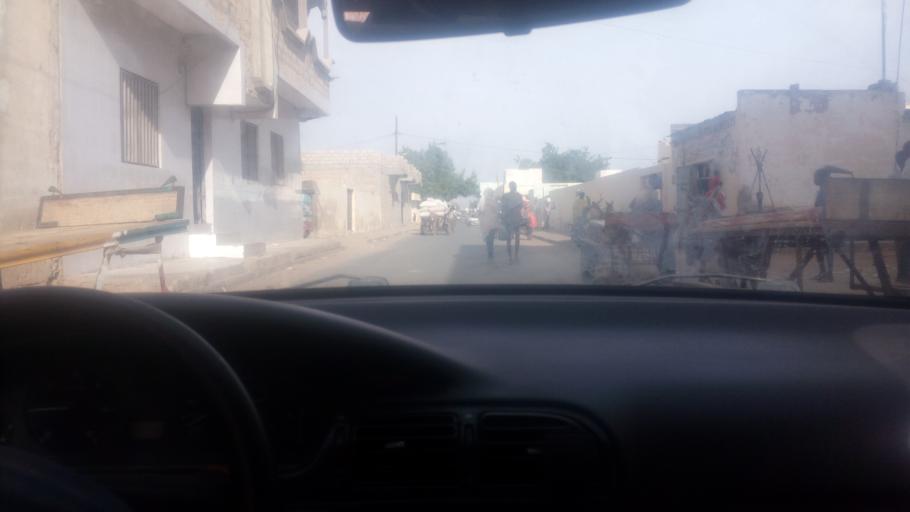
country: SN
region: Diourbel
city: Touba
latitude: 14.8552
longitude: -15.8935
